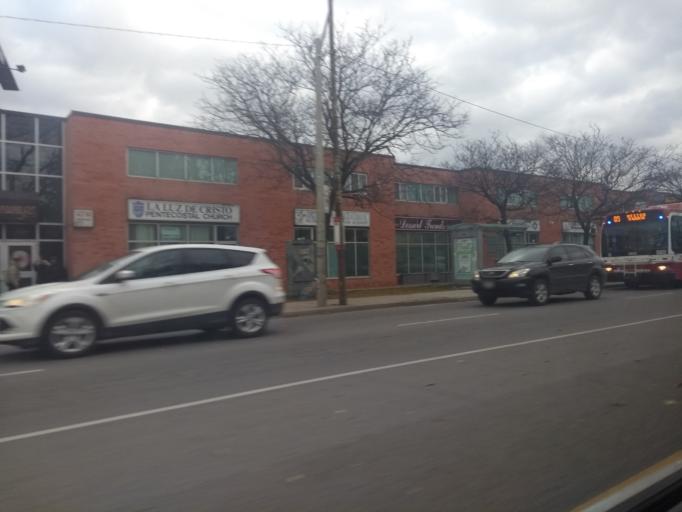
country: CA
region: Ontario
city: Toronto
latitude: 43.6788
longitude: -79.4738
